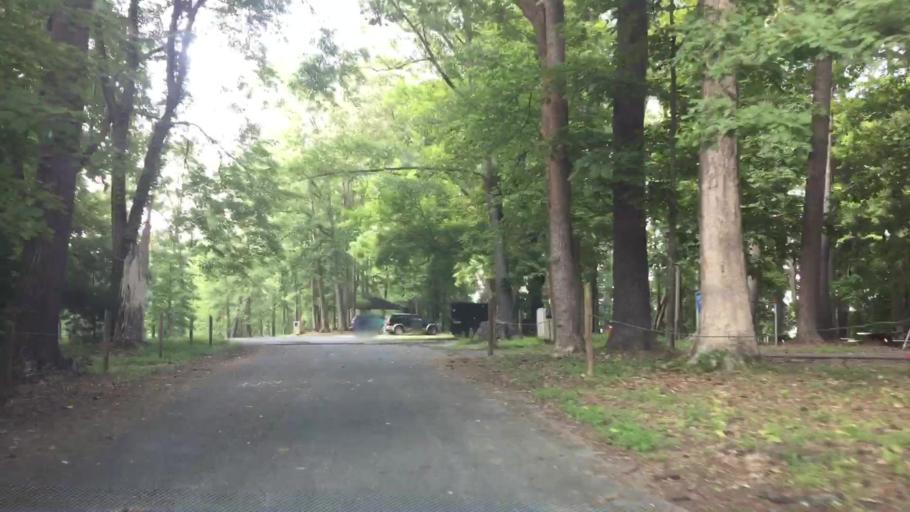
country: US
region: Tennessee
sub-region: Sullivan County
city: Fairmount
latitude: 36.5786
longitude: -82.0399
